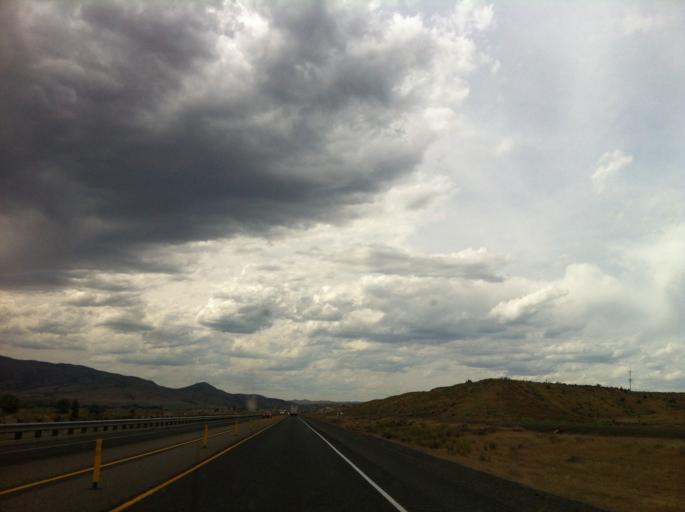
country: US
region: Oregon
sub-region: Baker County
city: Baker City
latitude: 44.5570
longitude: -117.4266
